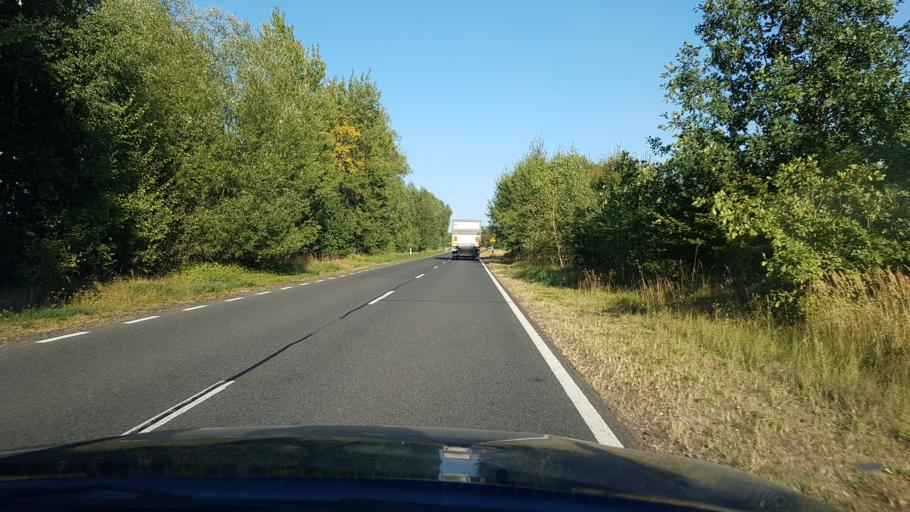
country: PL
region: West Pomeranian Voivodeship
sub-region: Powiat stargardzki
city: Marianowo
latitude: 53.4280
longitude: 15.2423
